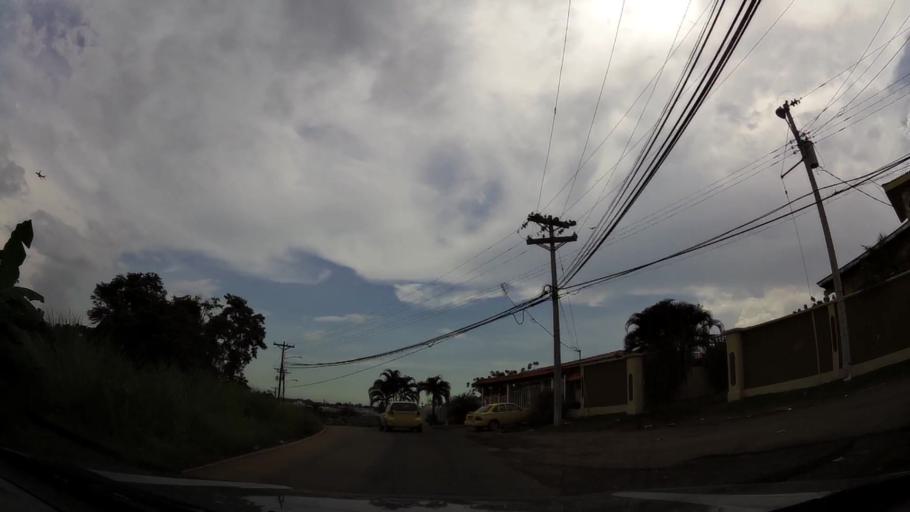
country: PA
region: Panama
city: Tocumen
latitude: 9.1105
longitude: -79.3724
